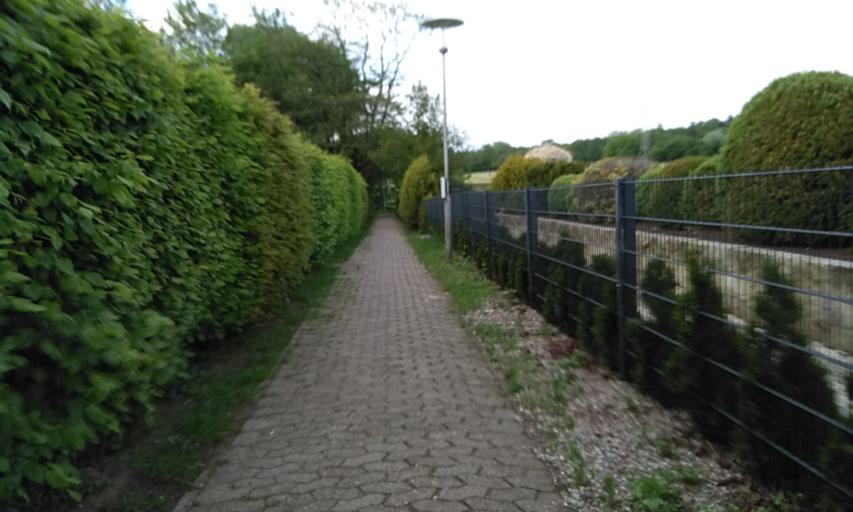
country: DE
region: Lower Saxony
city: Harsefeld
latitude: 53.4596
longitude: 9.4872
